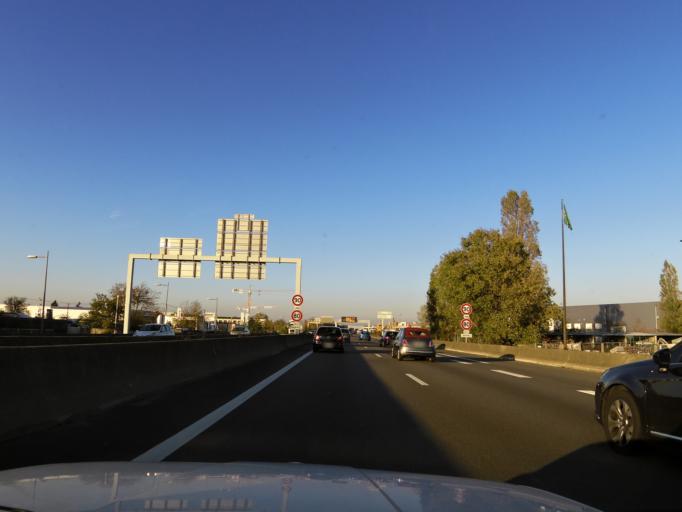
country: FR
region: Rhone-Alpes
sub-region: Departement du Rhone
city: Chassieu
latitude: 45.7163
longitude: 4.9705
